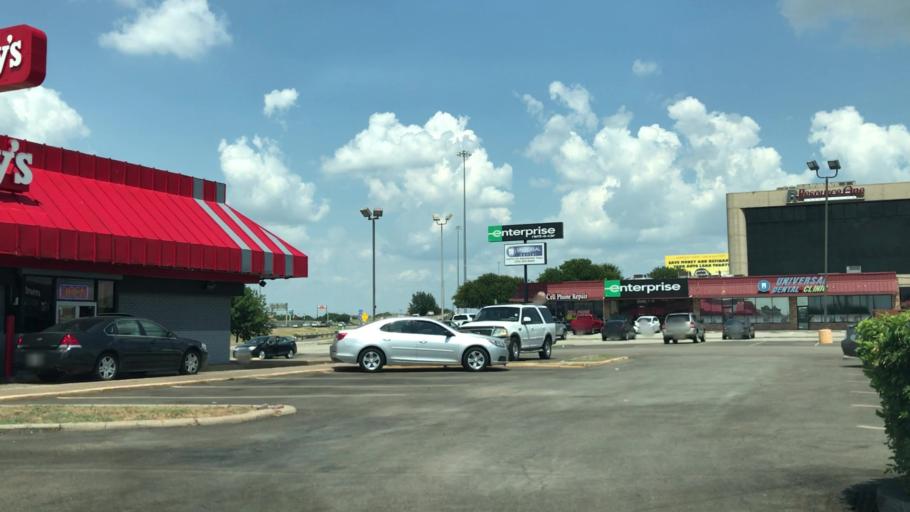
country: US
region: Texas
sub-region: Dallas County
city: Balch Springs
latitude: 32.7930
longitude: -96.6993
